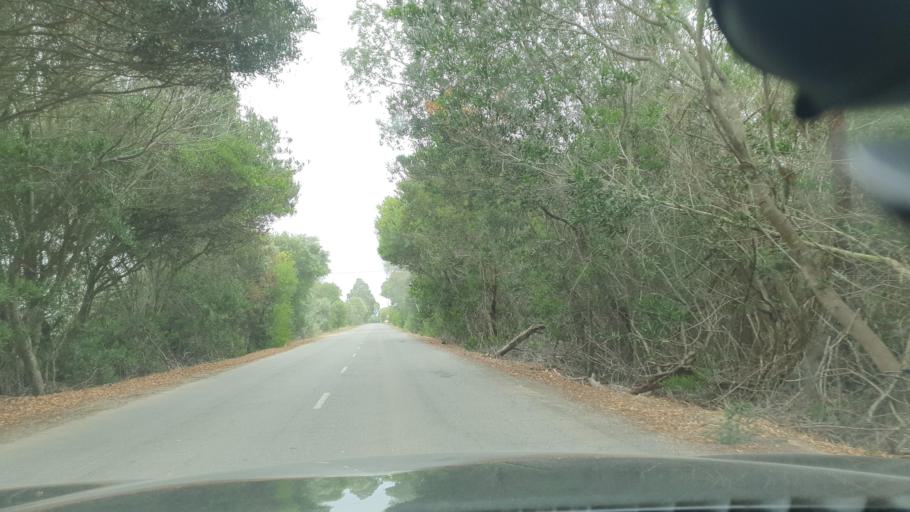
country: PT
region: Beja
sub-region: Odemira
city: Sao Teotonio
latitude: 37.4995
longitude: -8.6846
